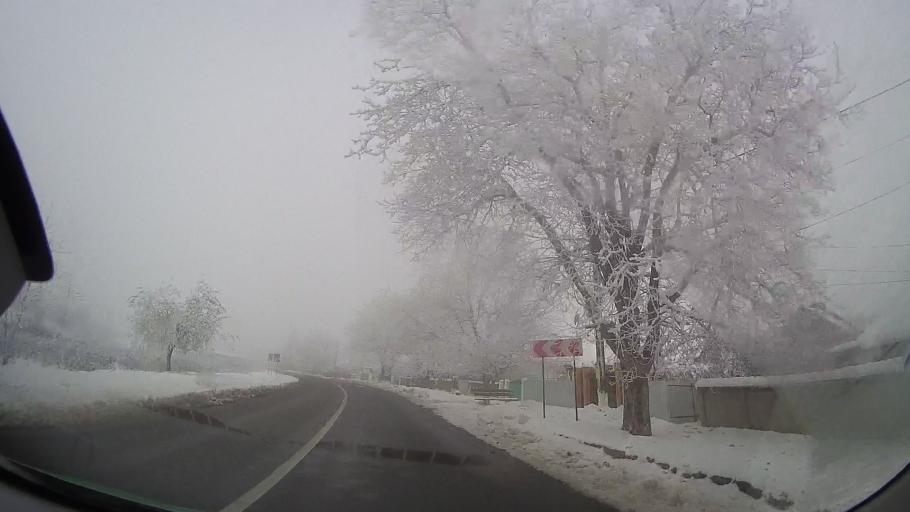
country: RO
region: Iasi
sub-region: Comuna Mircesti
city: Mircesti
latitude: 47.0910
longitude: 26.8222
